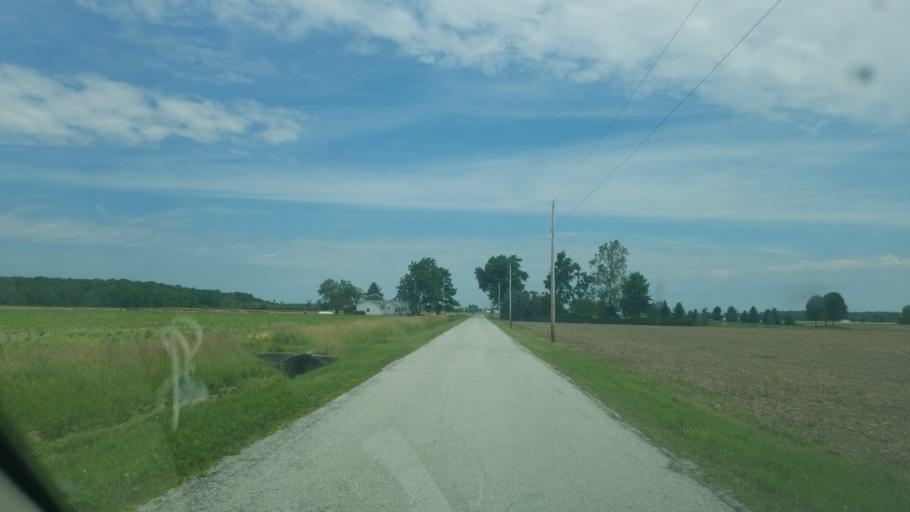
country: US
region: Ohio
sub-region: Wood County
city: North Baltimore
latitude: 41.2191
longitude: -83.5731
